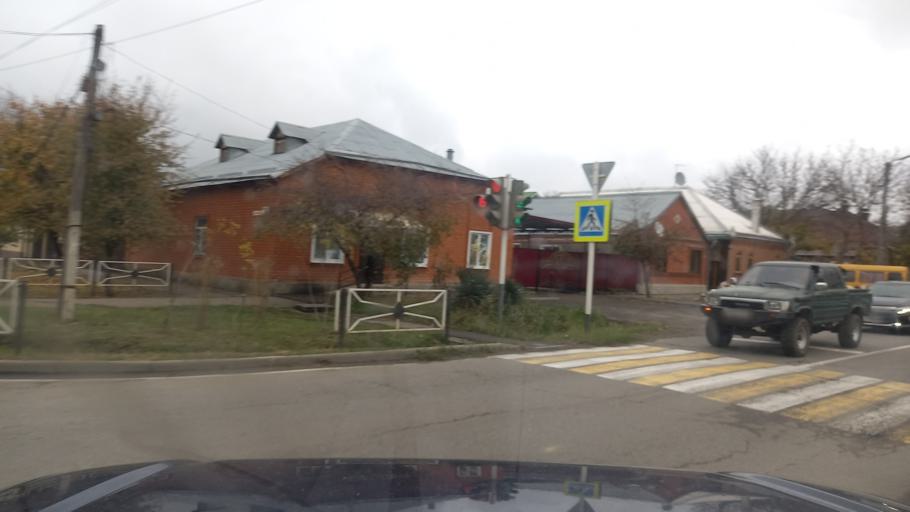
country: RU
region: Adygeya
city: Maykop
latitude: 44.6078
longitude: 40.0719
